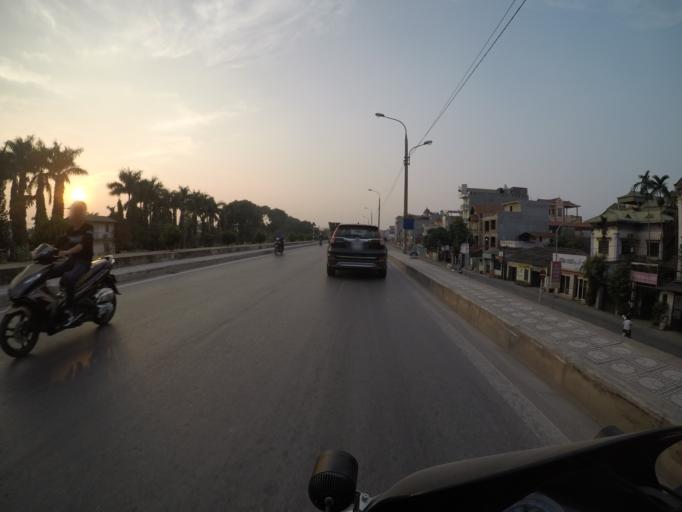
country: VN
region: Ha Noi
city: Hoan Kiem
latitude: 21.0329
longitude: 105.8767
